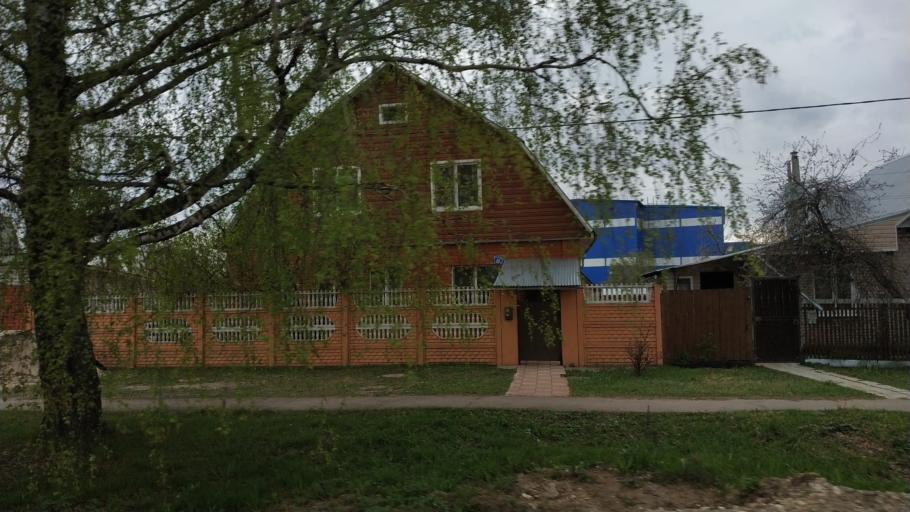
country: RU
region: Moskovskaya
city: Pavlovskiy Posad
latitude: 55.7704
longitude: 38.6936
